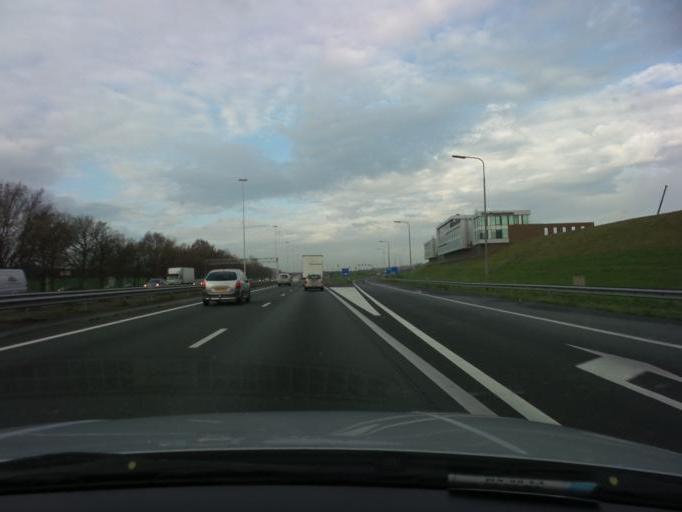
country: NL
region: Utrecht
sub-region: Gemeente Amersfoort
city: Hoogland
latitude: 52.1905
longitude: 5.4081
